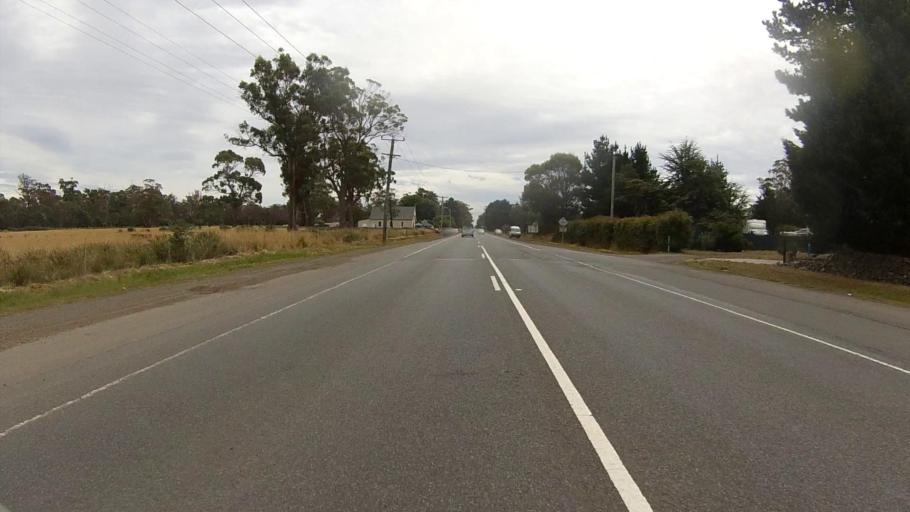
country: AU
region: Tasmania
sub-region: Northern Midlands
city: Evandale
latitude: -41.7594
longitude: 147.3507
